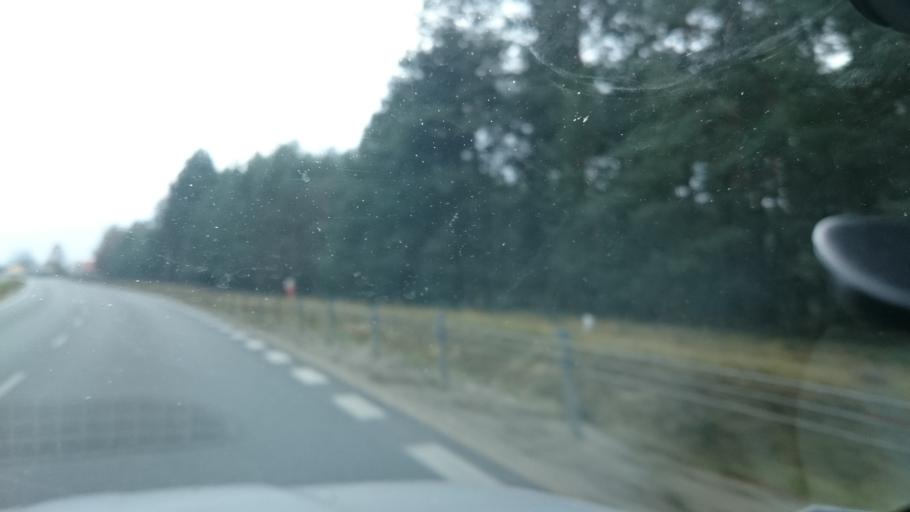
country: PL
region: Swietokrzyskie
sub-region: Powiat konecki
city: Konskie
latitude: 51.1507
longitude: 20.3616
